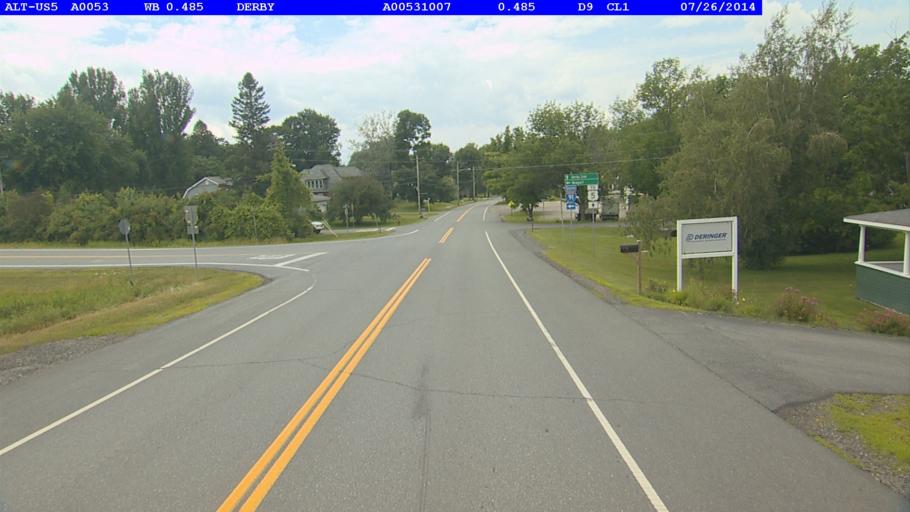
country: US
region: Vermont
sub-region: Orleans County
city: Newport
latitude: 45.0052
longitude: -72.0900
